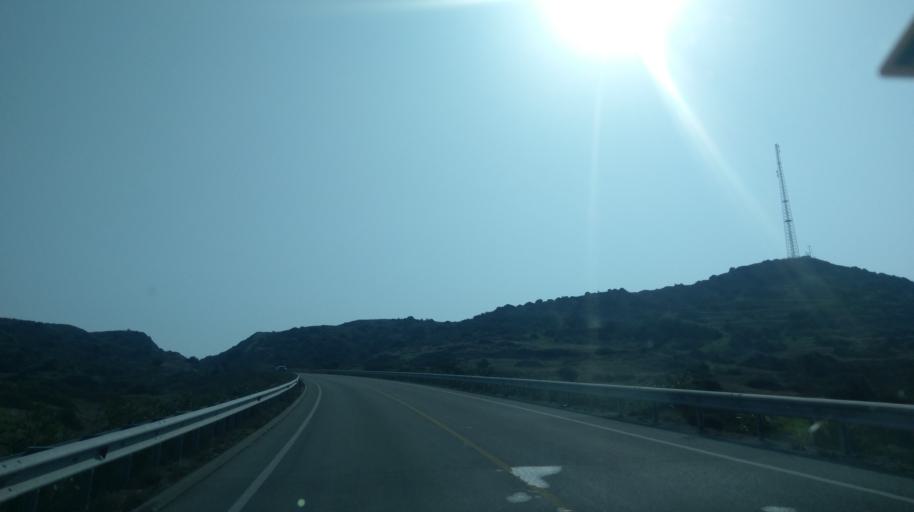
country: CY
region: Ammochostos
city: Leonarisso
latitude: 35.4912
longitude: 34.0980
